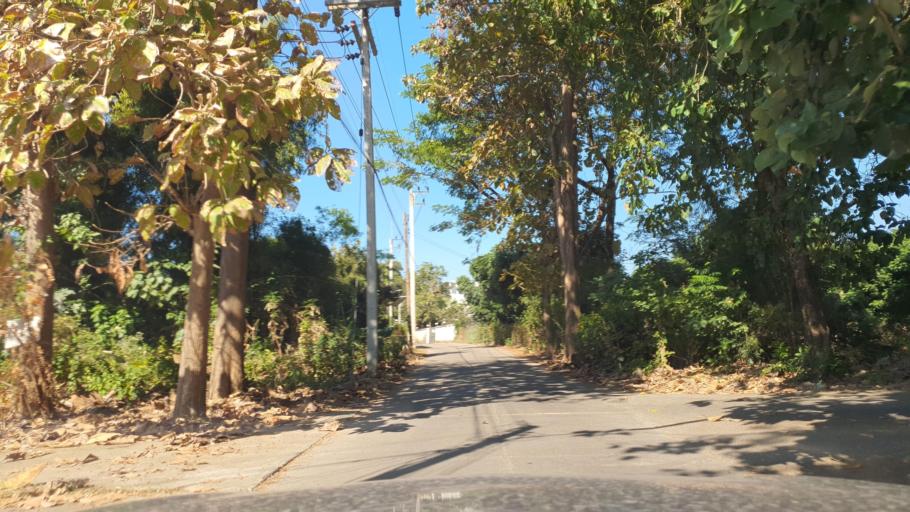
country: TH
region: Chiang Mai
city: Hang Dong
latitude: 18.6809
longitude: 98.9236
